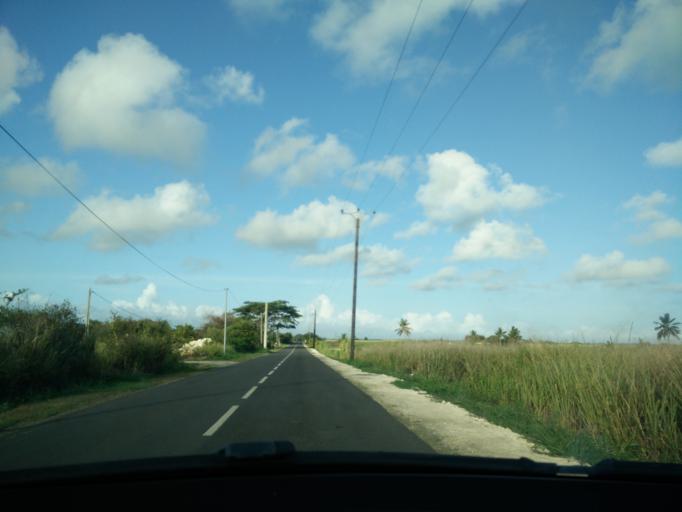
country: GP
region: Guadeloupe
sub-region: Guadeloupe
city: Le Moule
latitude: 16.3212
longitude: -61.3559
